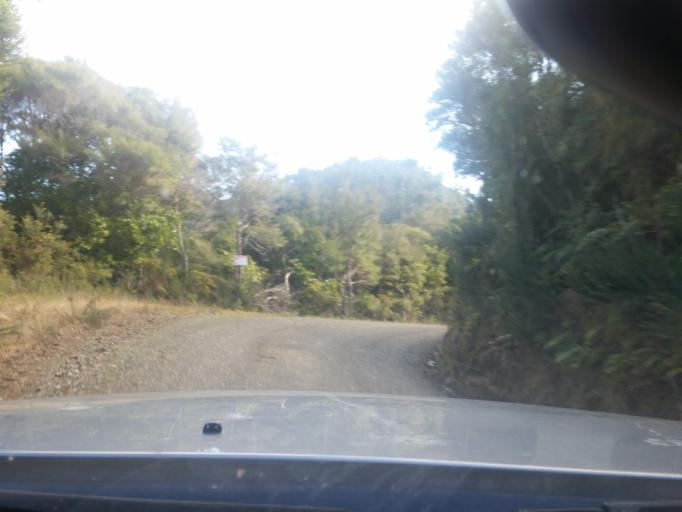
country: NZ
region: Tasman
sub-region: Tasman District
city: Takaka
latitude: -40.6263
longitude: 172.5036
